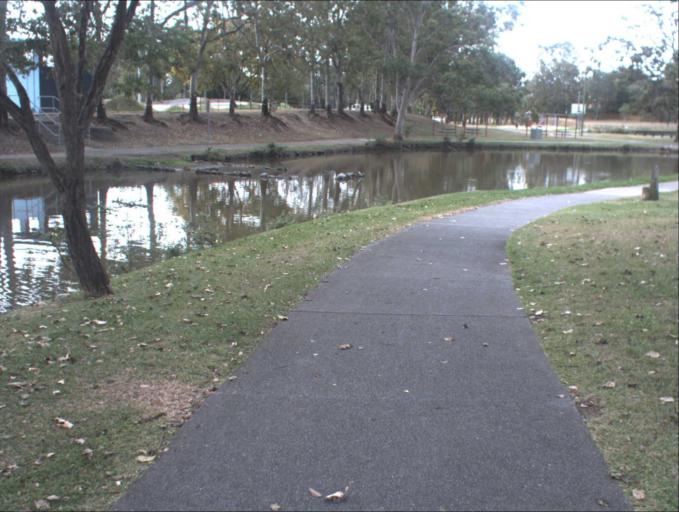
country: AU
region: Queensland
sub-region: Logan
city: Beenleigh
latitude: -27.7076
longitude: 153.1971
